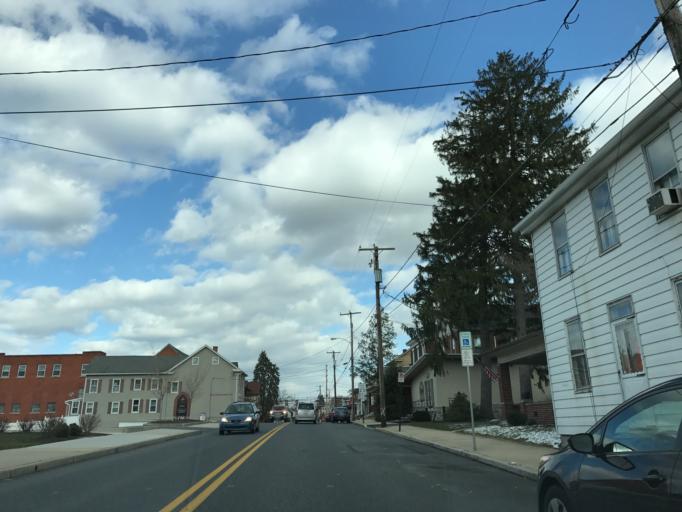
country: US
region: Pennsylvania
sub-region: Lancaster County
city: Elizabethtown
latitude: 40.1523
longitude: -76.6039
